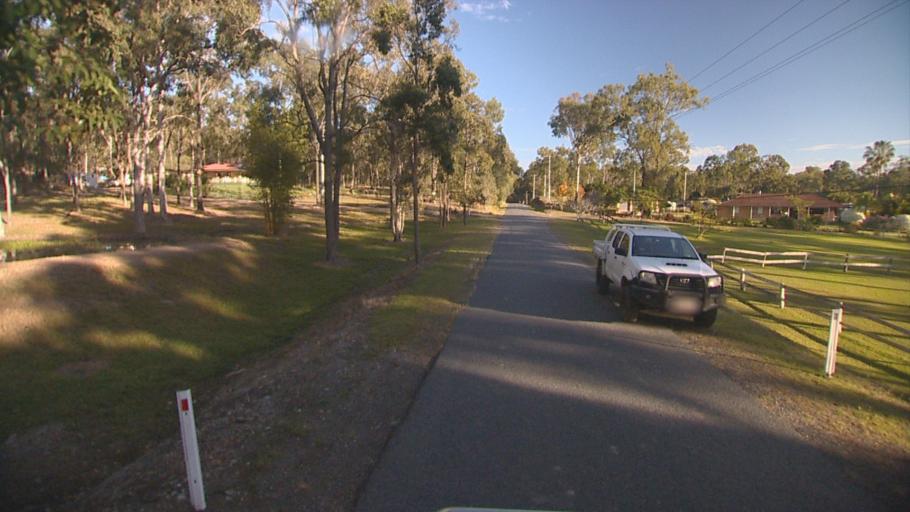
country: AU
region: Queensland
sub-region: Logan
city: Waterford West
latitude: -27.7335
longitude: 153.1516
